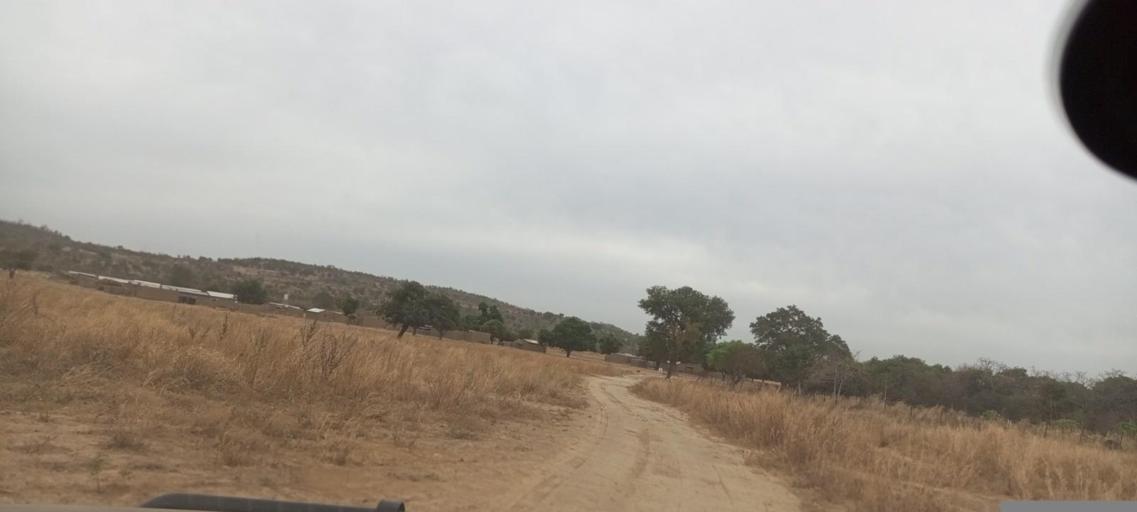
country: ML
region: Koulikoro
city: Kati
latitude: 12.7638
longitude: -8.4044
